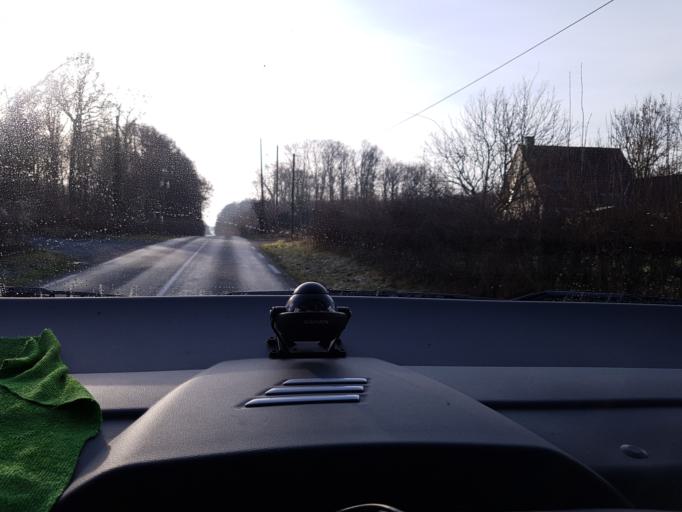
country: FR
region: Nord-Pas-de-Calais
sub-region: Departement du Nord
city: La Longueville
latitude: 50.2614
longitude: 3.8243
